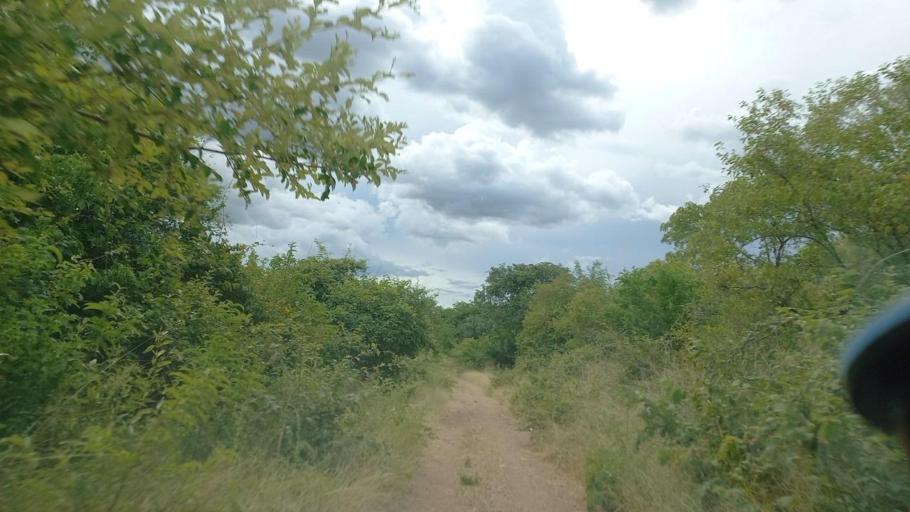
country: ZM
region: Lusaka
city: Luangwa
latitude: -15.6484
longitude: 30.3382
